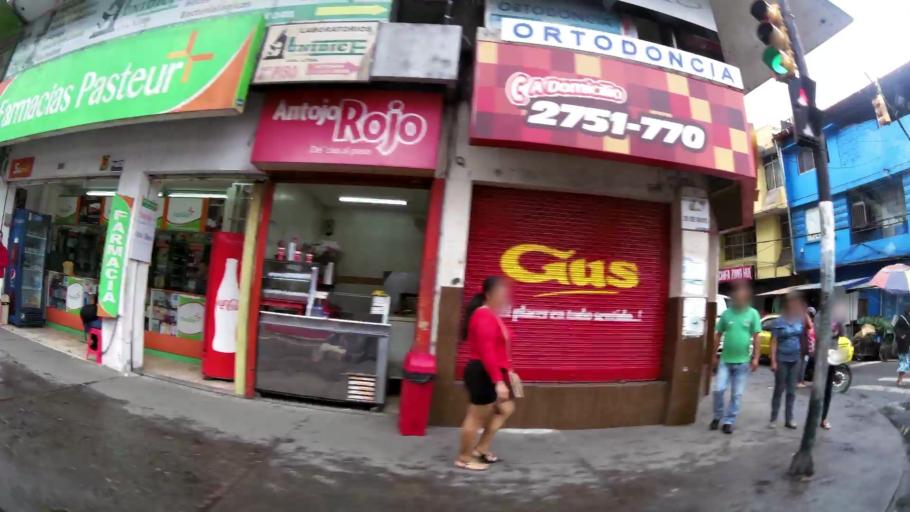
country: EC
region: Santo Domingo de los Tsachilas
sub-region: Canton Santo Domingo de los Colorados
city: Santo Domingo de los Colorados
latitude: -0.2538
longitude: -79.1708
